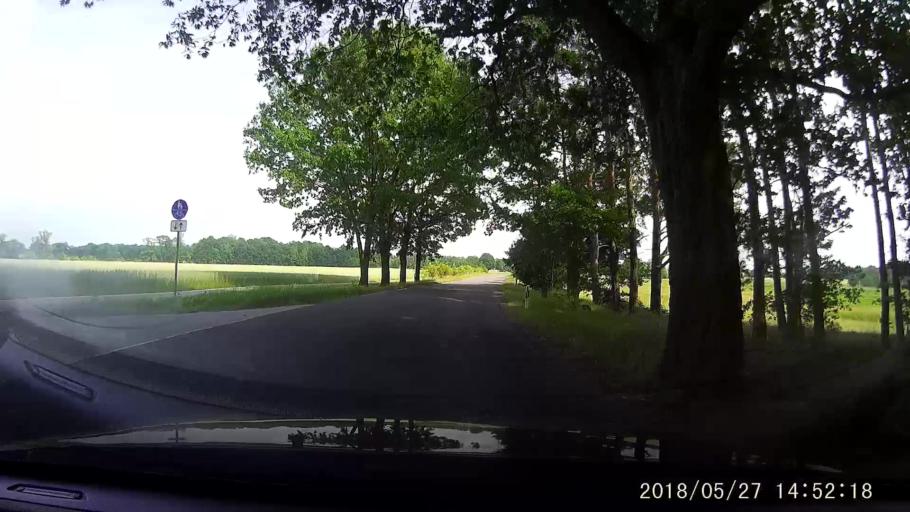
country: DE
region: Saxony
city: Klitten
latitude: 51.3571
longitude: 14.5812
